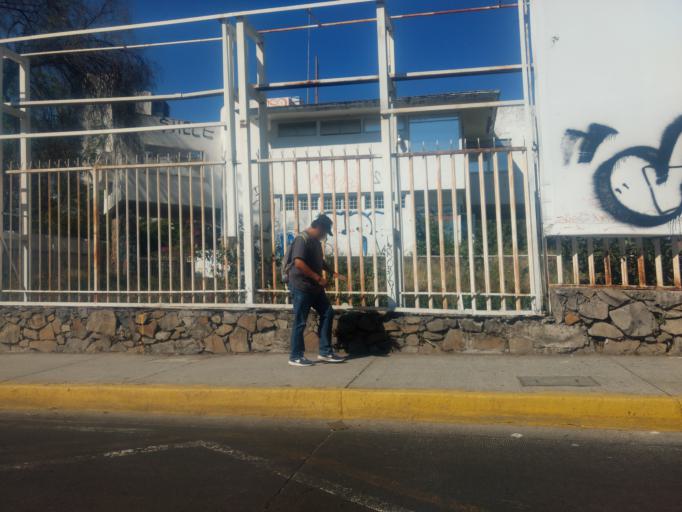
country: MX
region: Jalisco
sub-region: Zapopan
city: Zapopan
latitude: 20.6989
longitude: -103.3742
